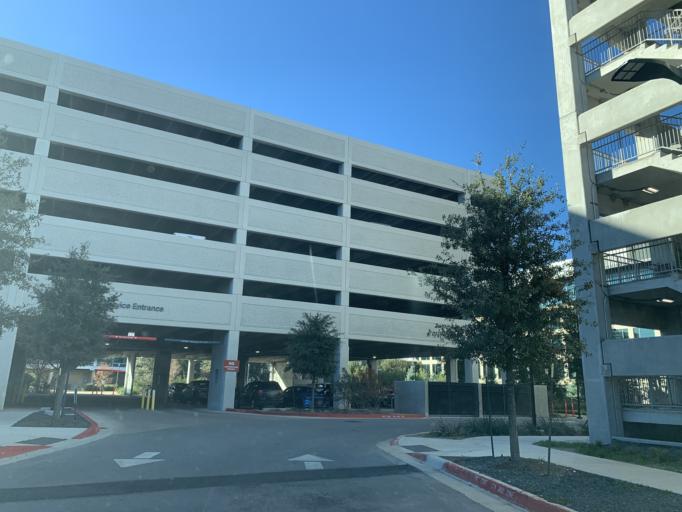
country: US
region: Texas
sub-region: Travis County
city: Wells Branch
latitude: 30.3989
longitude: -97.7109
